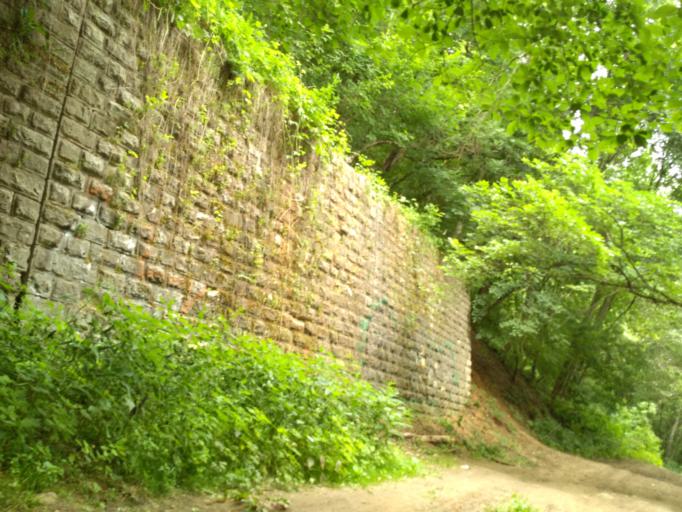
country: RU
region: Nizjnij Novgorod
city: Nizhniy Novgorod
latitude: 56.2798
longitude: 43.9706
